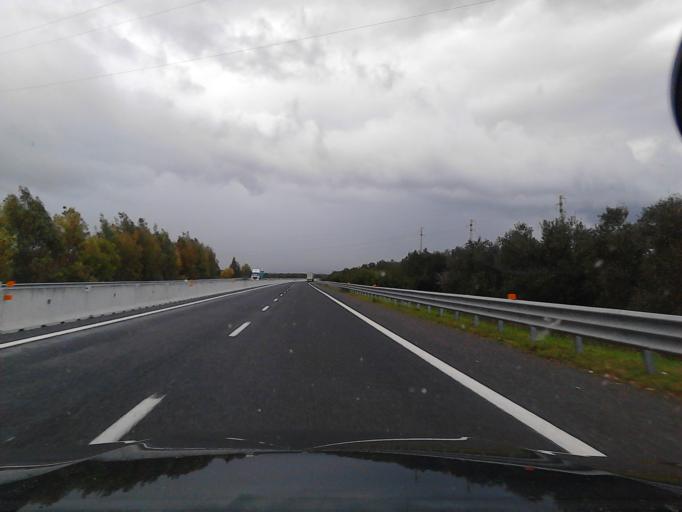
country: IT
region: Apulia
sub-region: Provincia di Bari
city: Modugno
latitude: 41.1005
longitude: 16.7547
